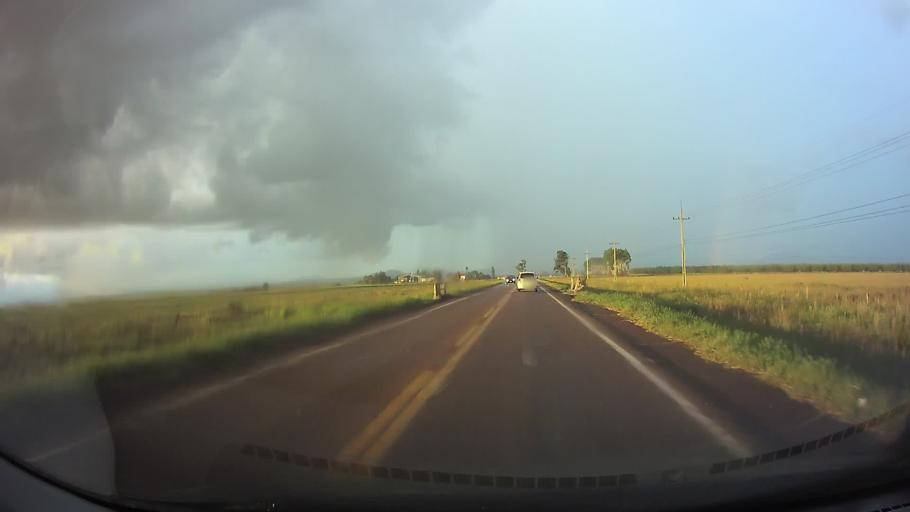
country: PY
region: Paraguari
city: Paraguari
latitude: -25.6826
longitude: -57.1678
